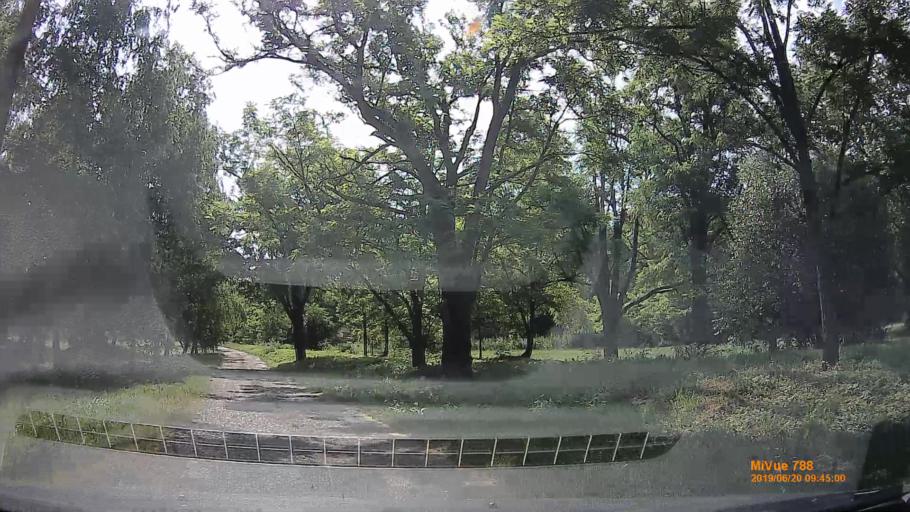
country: HU
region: Baranya
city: Pecsvarad
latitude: 46.1737
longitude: 18.4686
